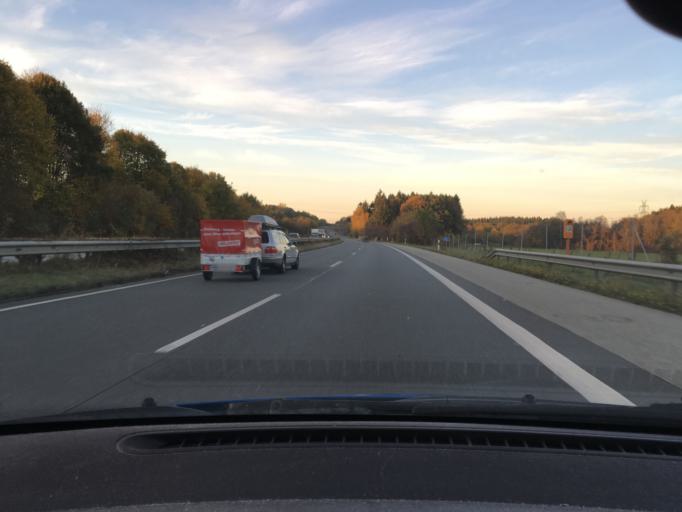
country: DE
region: Schleswig-Holstein
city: Neversdorf
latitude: 53.8400
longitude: 10.3097
